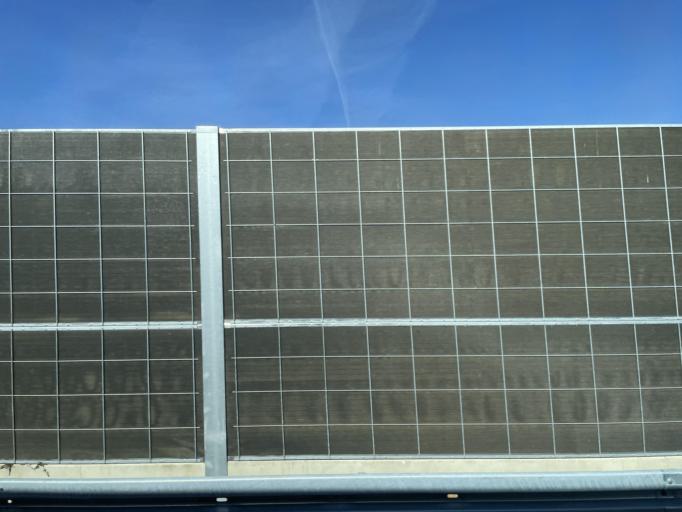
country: BA
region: Federation of Bosnia and Herzegovina
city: Pazaric
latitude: 43.7899
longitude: 18.0795
